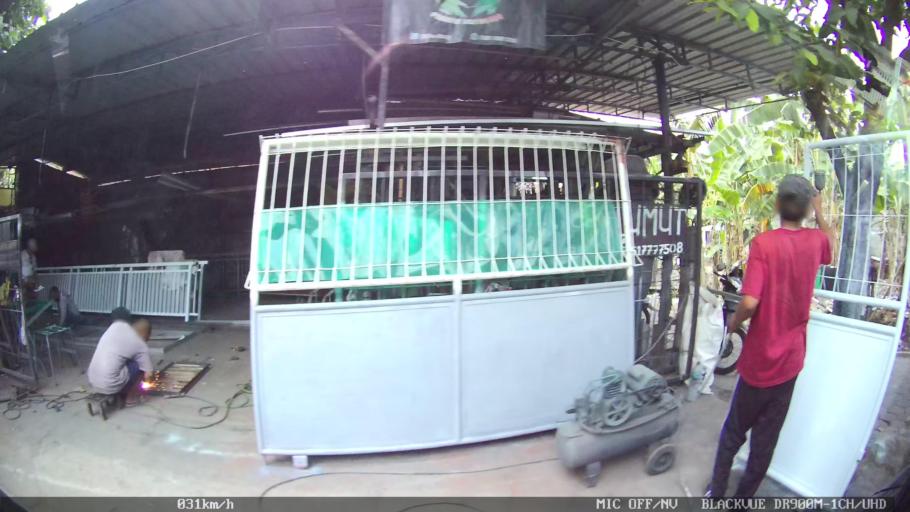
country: ID
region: Daerah Istimewa Yogyakarta
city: Yogyakarta
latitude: -7.8165
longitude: 110.3982
